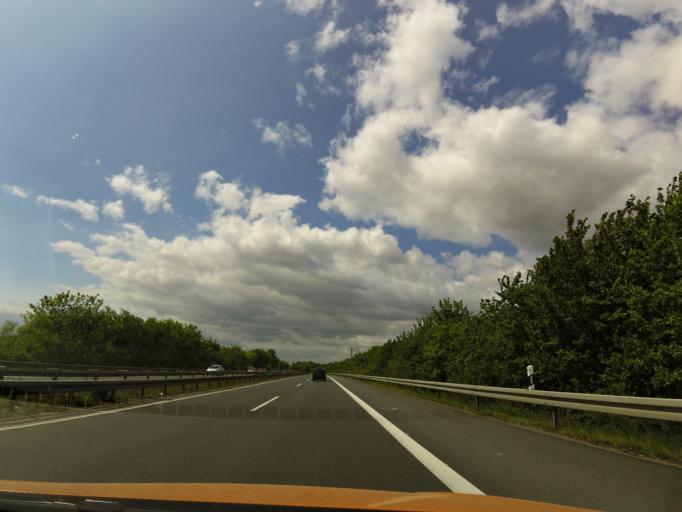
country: DE
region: Lower Saxony
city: Vechelde
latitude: 52.1962
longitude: 10.4217
